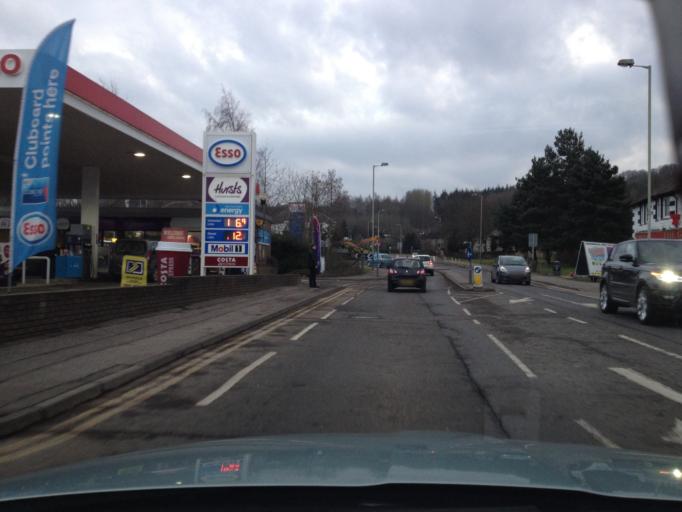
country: GB
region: Scotland
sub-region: Perth and Kinross
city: Perth
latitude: 56.3810
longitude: -3.4346
